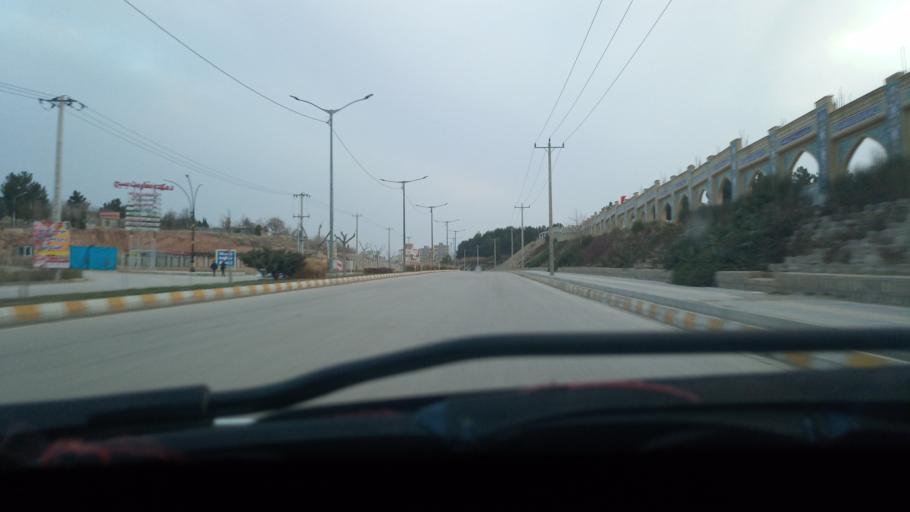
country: IR
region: Khorasan-e Shomali
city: Bojnurd
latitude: 37.4594
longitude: 57.3315
